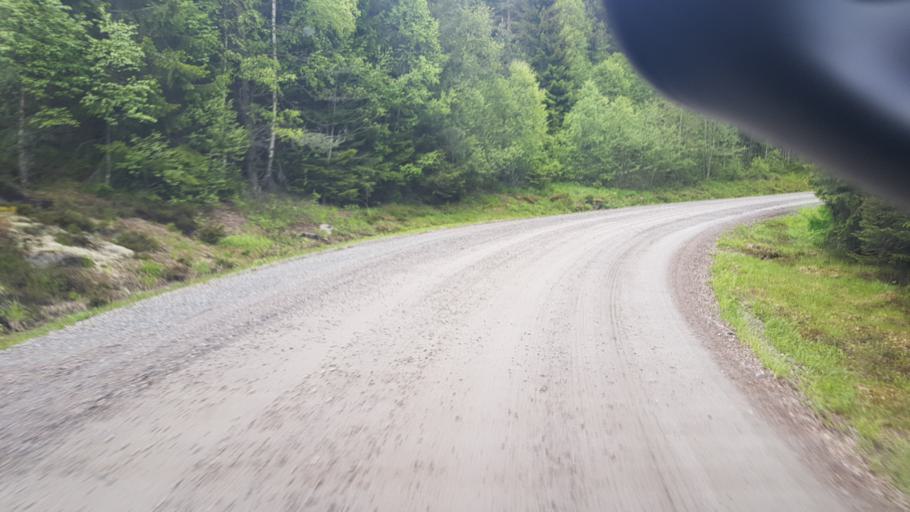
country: NO
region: Ostfold
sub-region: Romskog
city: Romskog
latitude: 59.7122
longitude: 12.0281
